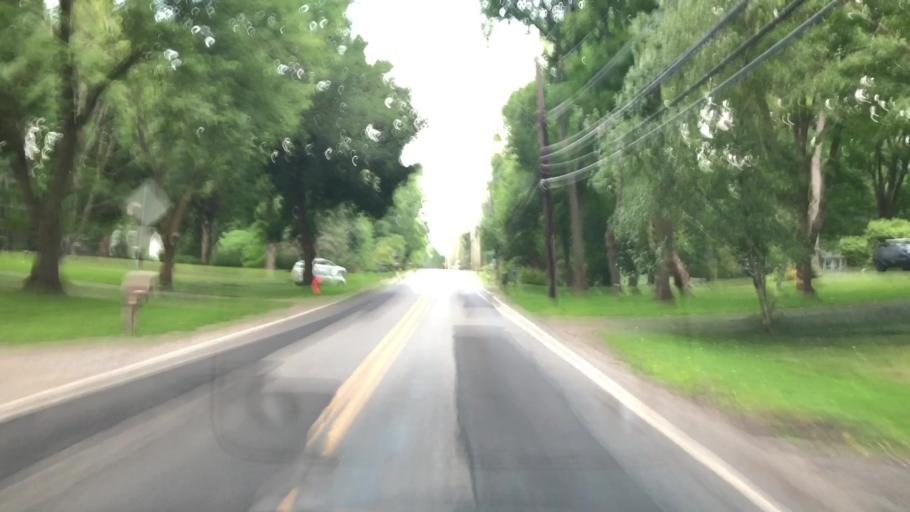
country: US
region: New York
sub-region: Erie County
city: East Aurora
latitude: 42.7739
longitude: -78.6069
